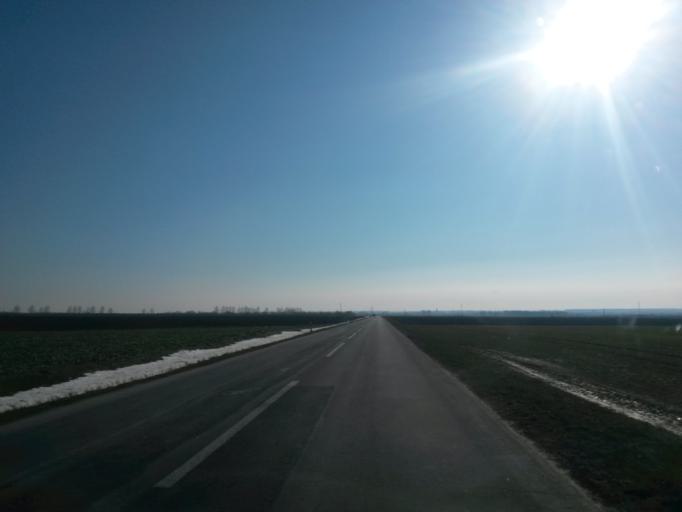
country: HR
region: Osjecko-Baranjska
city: Dalj
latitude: 45.5080
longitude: 18.9394
